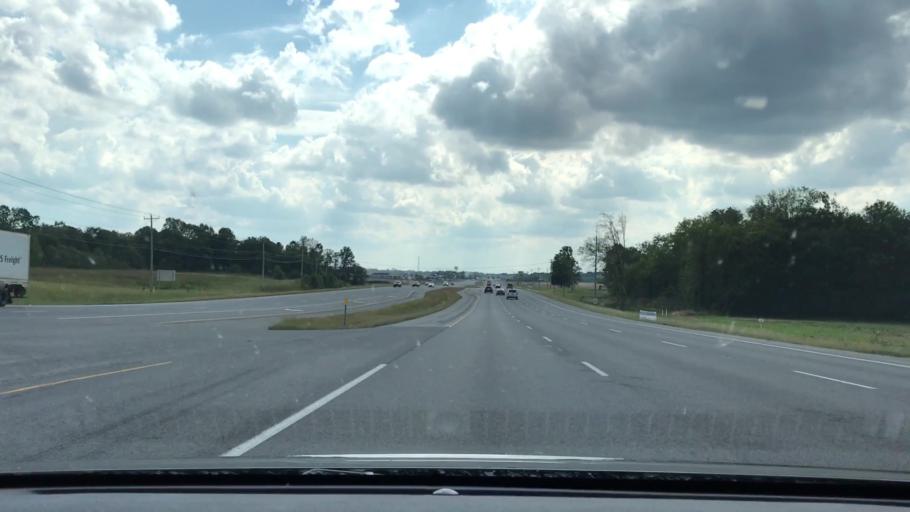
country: US
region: Kentucky
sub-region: Christian County
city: Oak Grove
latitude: 36.6818
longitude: -87.4484
